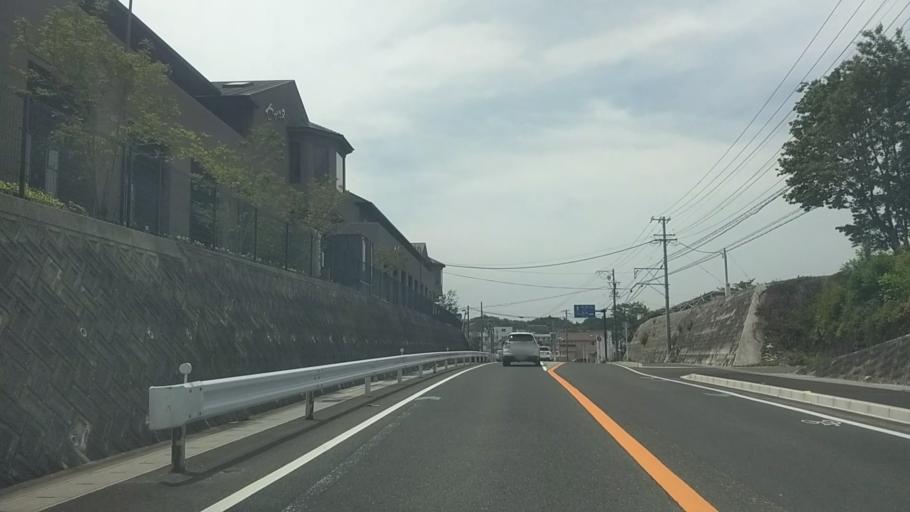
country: JP
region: Shizuoka
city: Kosai-shi
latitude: 34.7588
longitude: 137.5121
